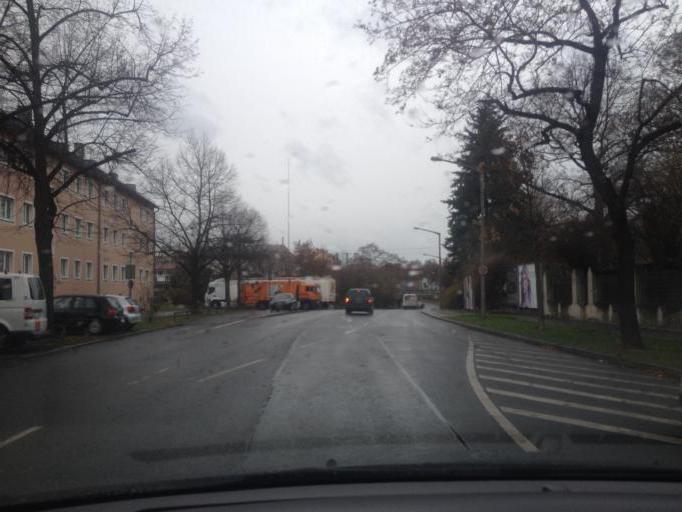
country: DE
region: Bavaria
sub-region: Regierungsbezirk Mittelfranken
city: Nuernberg
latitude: 49.4350
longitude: 11.0590
